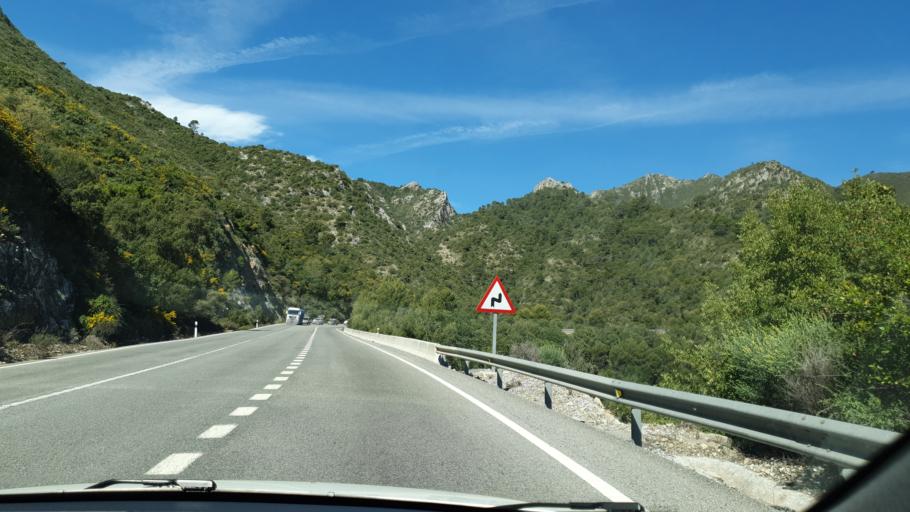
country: ES
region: Andalusia
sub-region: Provincia de Malaga
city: Ojen
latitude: 36.5661
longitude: -4.8625
